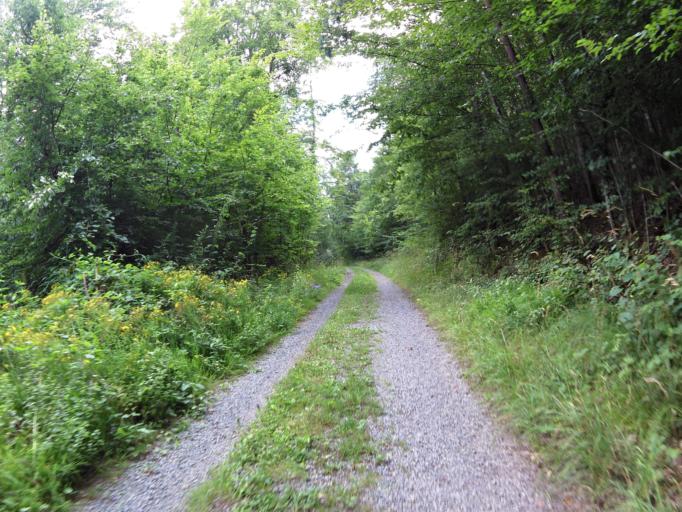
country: DE
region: Bavaria
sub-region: Regierungsbezirk Unterfranken
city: Thungersheim
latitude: 49.8871
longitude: 9.8701
